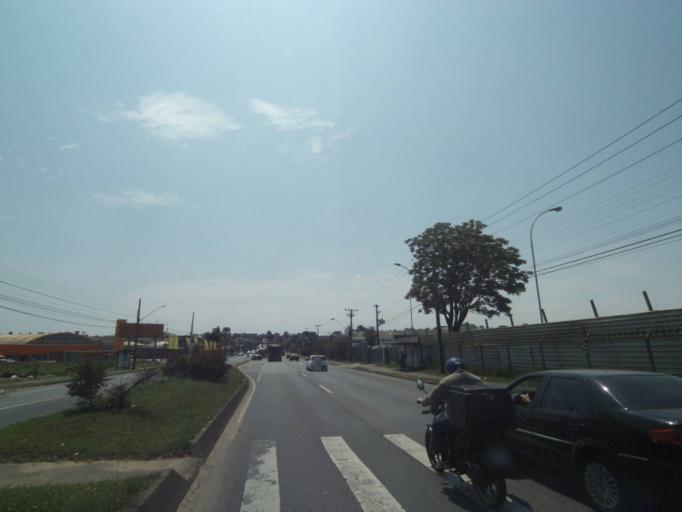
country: BR
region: Parana
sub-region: Curitiba
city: Curitiba
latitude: -25.4836
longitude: -49.3170
